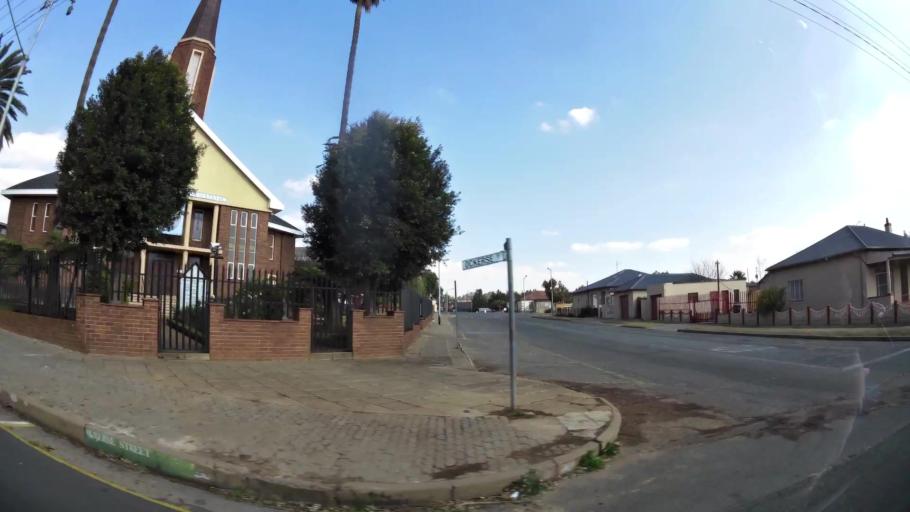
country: ZA
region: Gauteng
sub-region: West Rand District Municipality
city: Krugersdorp
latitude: -26.1012
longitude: 27.7674
